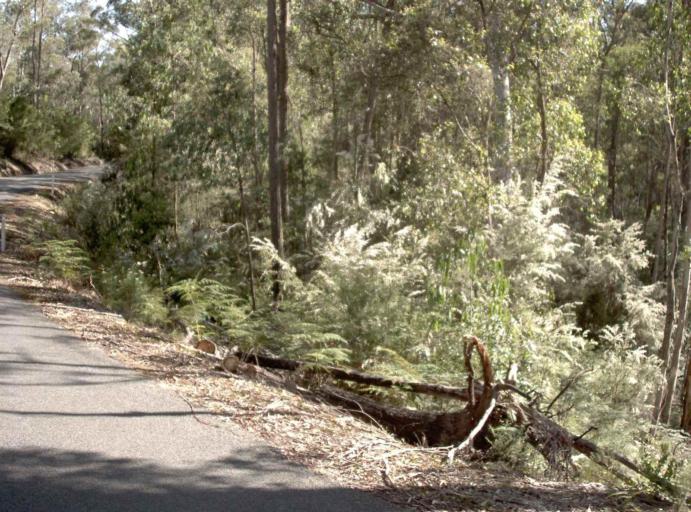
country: AU
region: Victoria
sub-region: East Gippsland
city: Lakes Entrance
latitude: -37.5114
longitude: 148.5439
